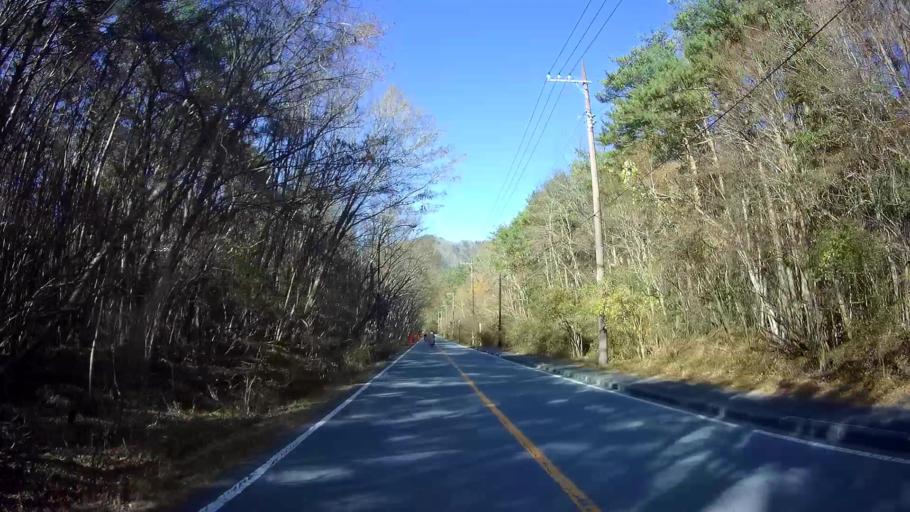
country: JP
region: Yamanashi
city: Fujikawaguchiko
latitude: 35.4692
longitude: 138.5988
